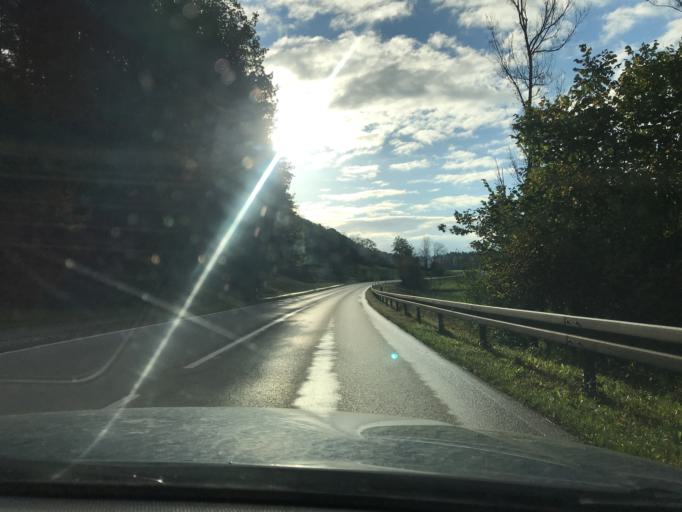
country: DE
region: Bavaria
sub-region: Upper Bavaria
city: Konigsdorf
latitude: 47.8243
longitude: 11.5372
